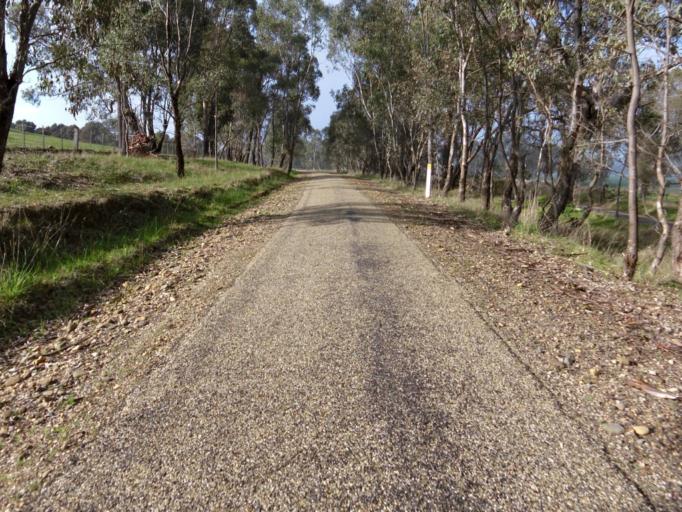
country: AU
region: Victoria
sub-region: Wangaratta
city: Wangaratta
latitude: -36.4485
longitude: 146.5515
